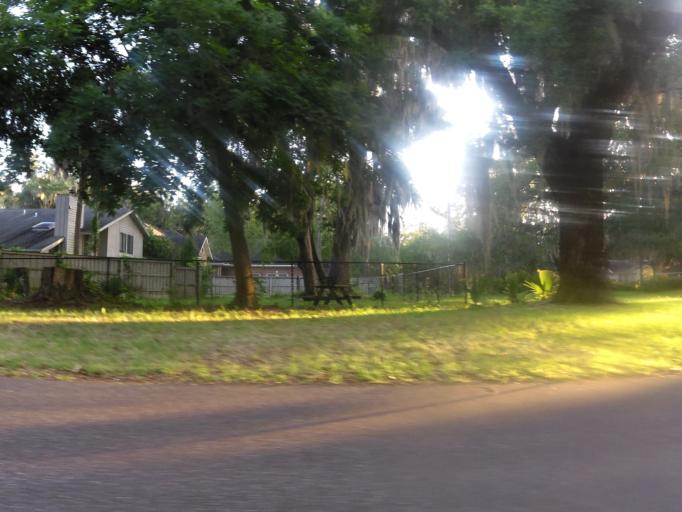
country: US
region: Florida
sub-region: Duval County
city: Jacksonville
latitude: 30.2686
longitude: -81.7077
